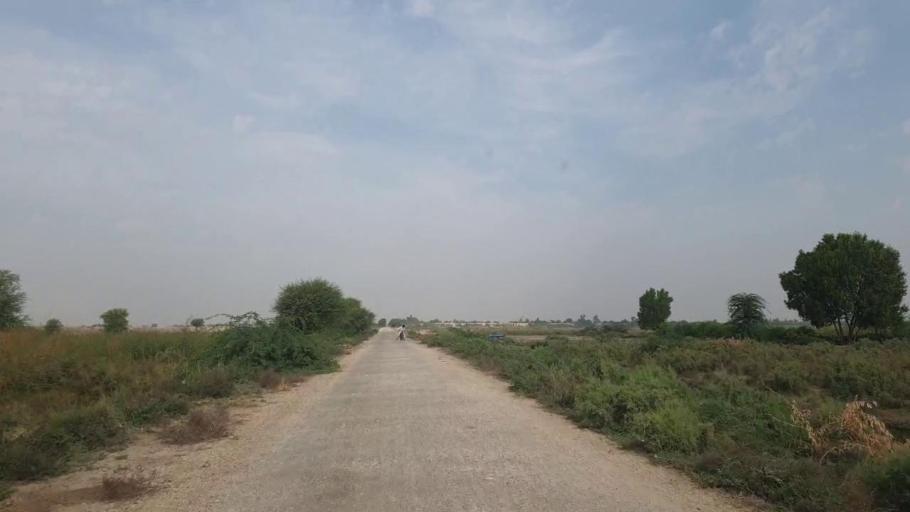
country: PK
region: Sindh
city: Rajo Khanani
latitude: 24.9821
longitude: 68.9951
